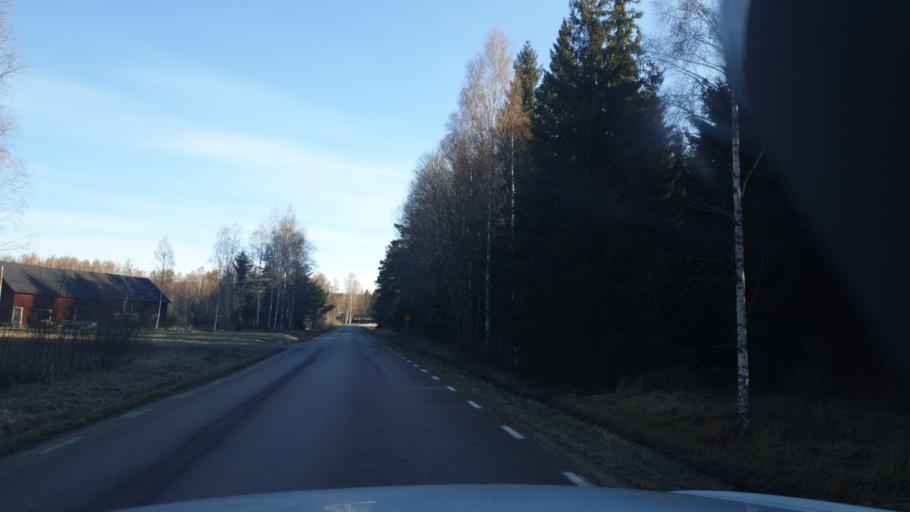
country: SE
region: Vaermland
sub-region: Arvika Kommun
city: Arvika
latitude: 59.5494
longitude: 12.7402
